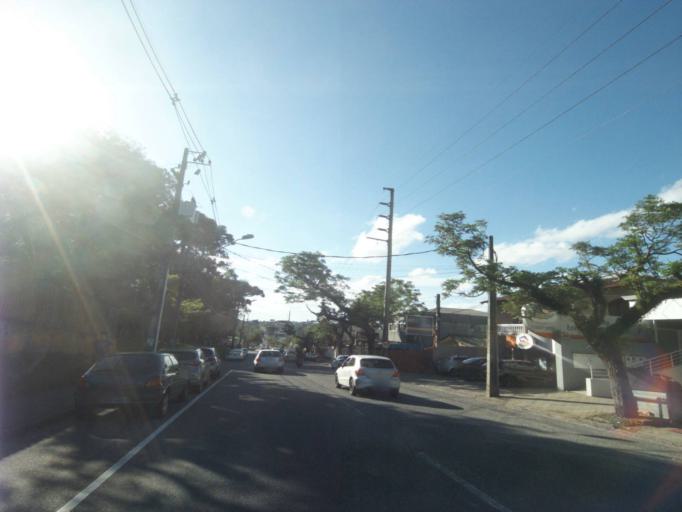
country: BR
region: Parana
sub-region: Curitiba
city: Curitiba
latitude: -25.3972
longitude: -49.2487
